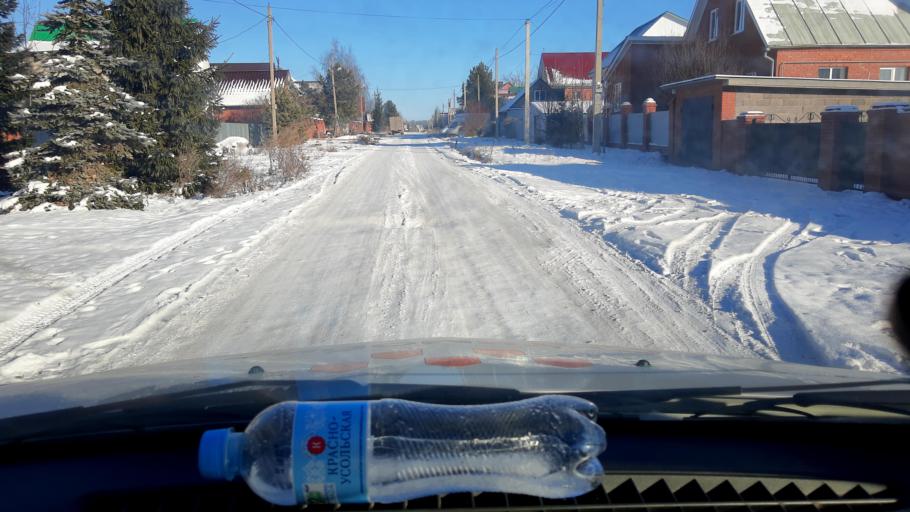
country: RU
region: Bashkortostan
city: Iglino
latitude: 54.7836
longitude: 56.2409
